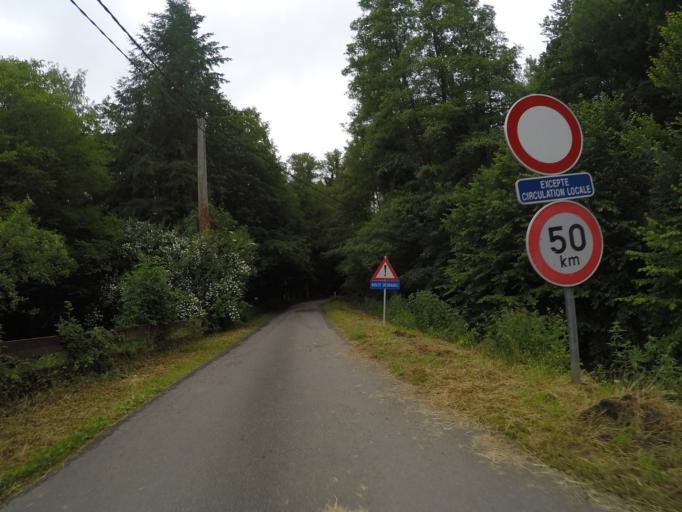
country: BE
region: Wallonia
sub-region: Province de Namur
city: Yvoir
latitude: 50.3333
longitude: 4.9283
